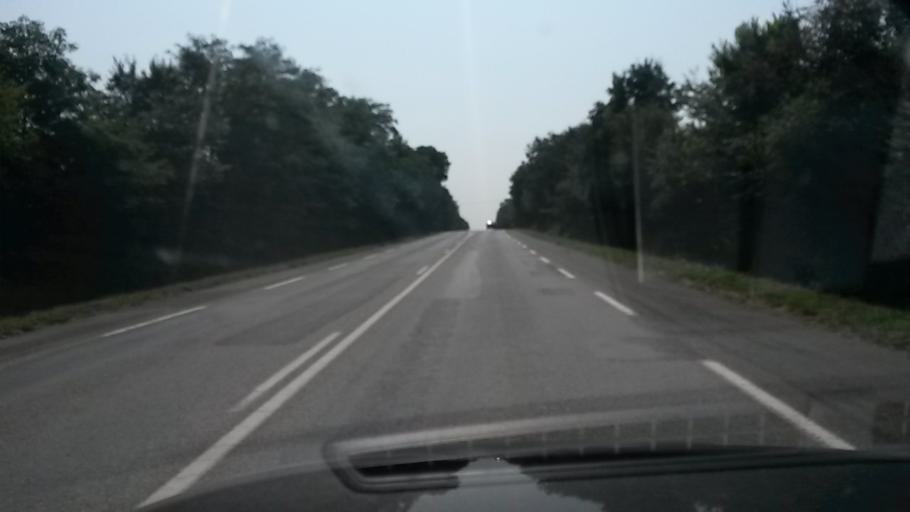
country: FR
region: Pays de la Loire
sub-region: Departement de la Mayenne
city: Chateau-Gontier
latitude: 47.8769
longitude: -0.6853
